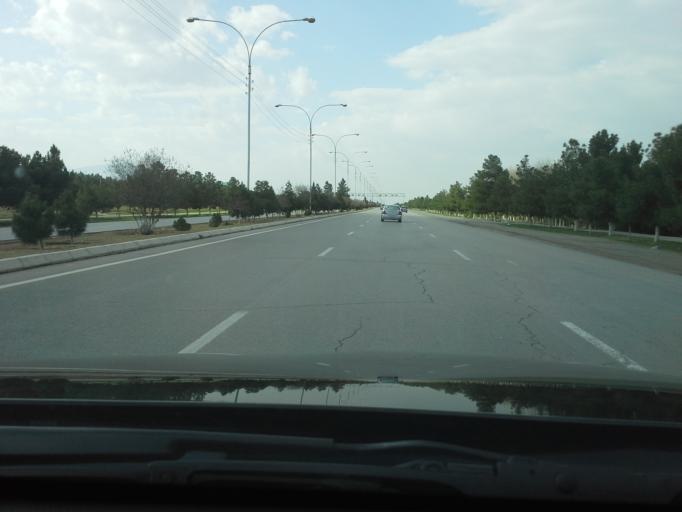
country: TM
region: Ahal
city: Ashgabat
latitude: 37.9624
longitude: 58.3125
